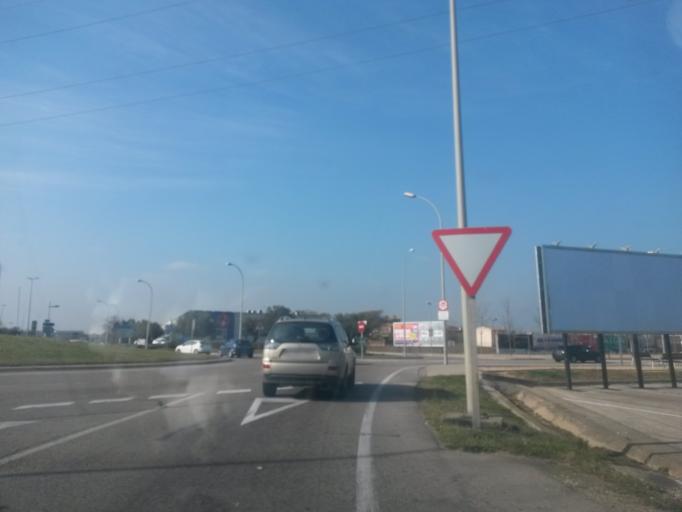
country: ES
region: Catalonia
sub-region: Provincia de Girona
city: Vila-sacra
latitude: 42.2676
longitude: 2.9996
